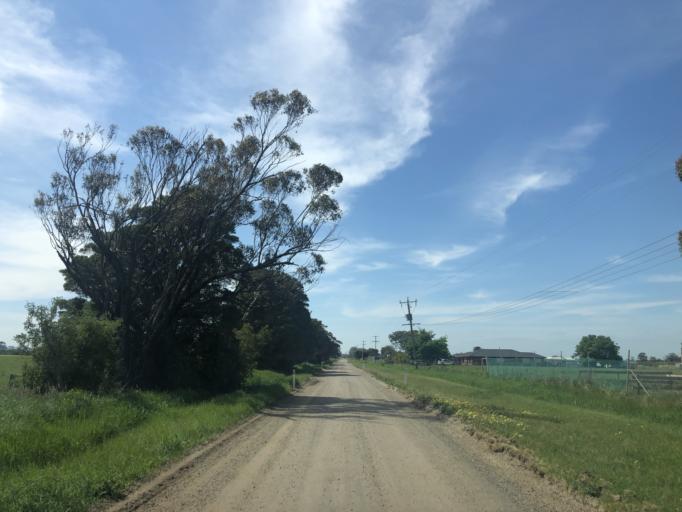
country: AU
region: Victoria
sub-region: Frankston
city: Sandhurst
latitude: -38.0564
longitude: 145.1904
